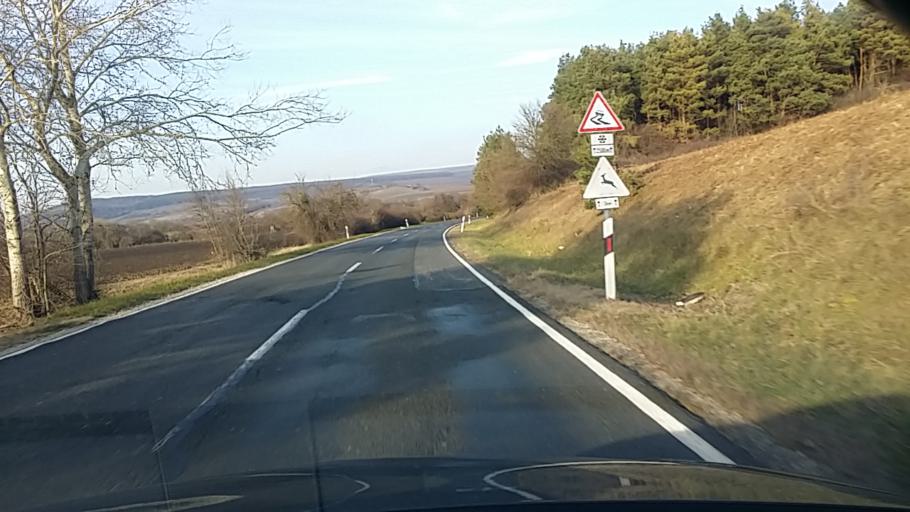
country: HU
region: Veszprem
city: Urkut
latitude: 46.9780
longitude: 17.6269
